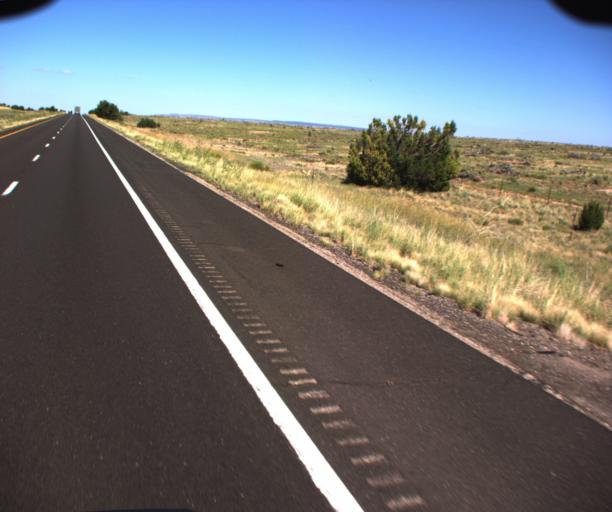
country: US
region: Arizona
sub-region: Yavapai County
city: Paulden
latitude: 35.2765
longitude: -112.7707
